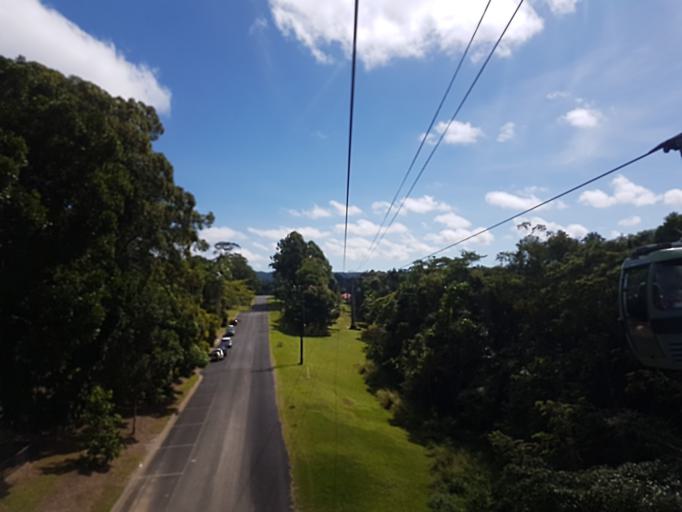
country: AU
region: Queensland
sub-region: Tablelands
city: Kuranda
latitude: -16.8225
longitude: 145.6406
